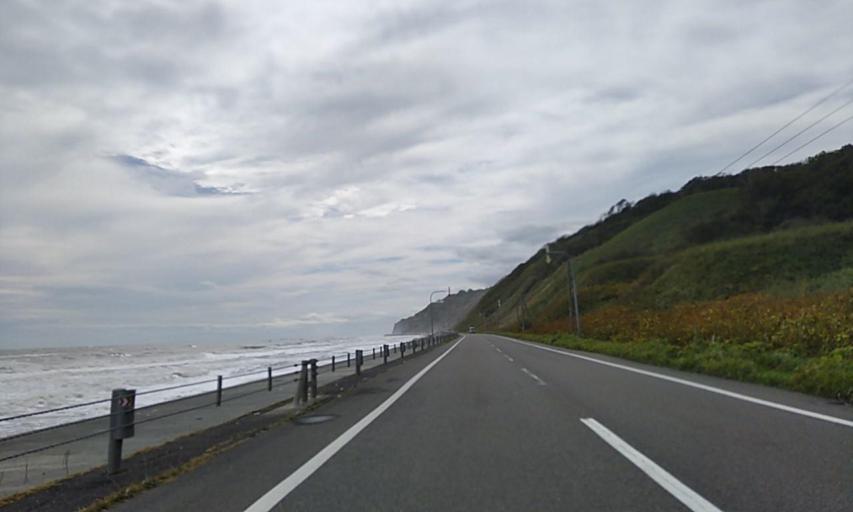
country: JP
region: Hokkaido
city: Obihiro
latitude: 42.7805
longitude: 143.7837
